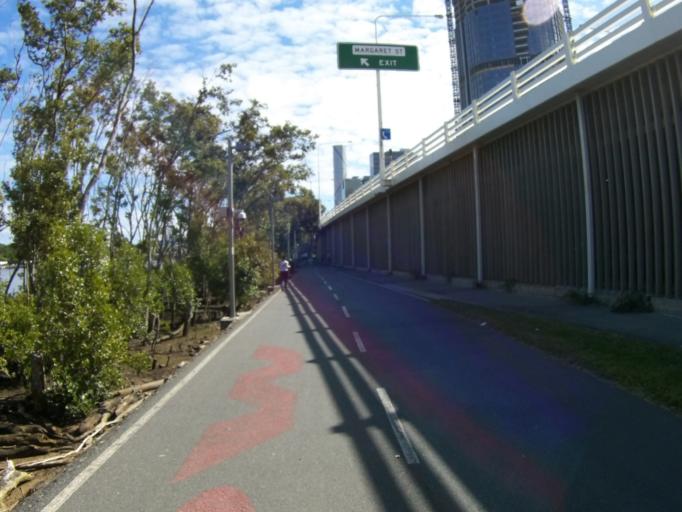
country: AU
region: Queensland
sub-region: Brisbane
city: South Brisbane
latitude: -27.4775
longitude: 153.0265
